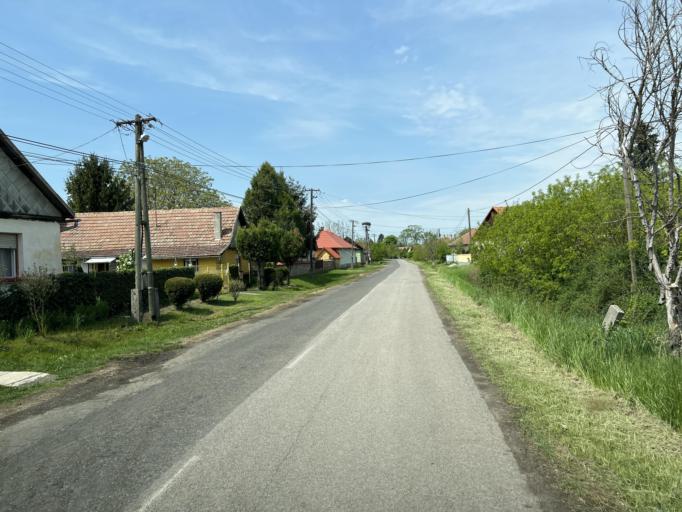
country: HU
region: Pest
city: Tapiogyorgye
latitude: 47.3414
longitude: 19.9506
